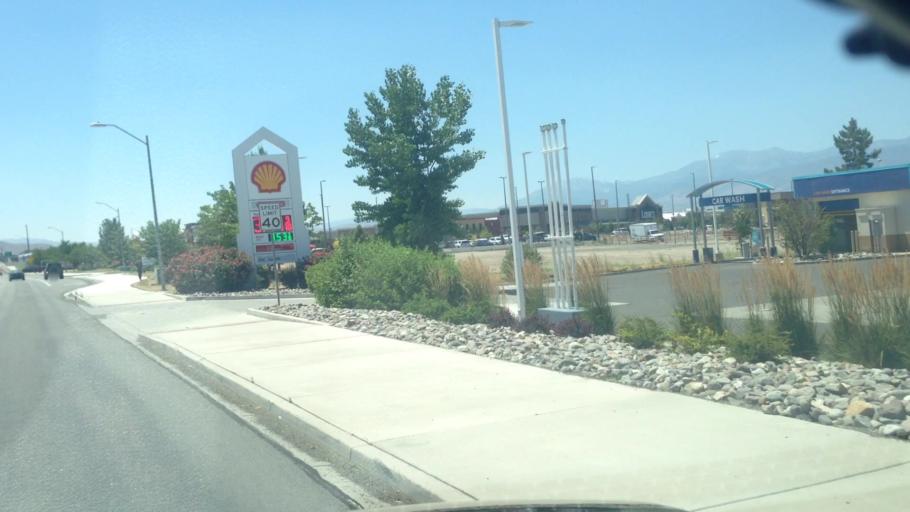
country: US
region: Nevada
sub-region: Washoe County
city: Sparks
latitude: 39.5332
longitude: -119.7128
